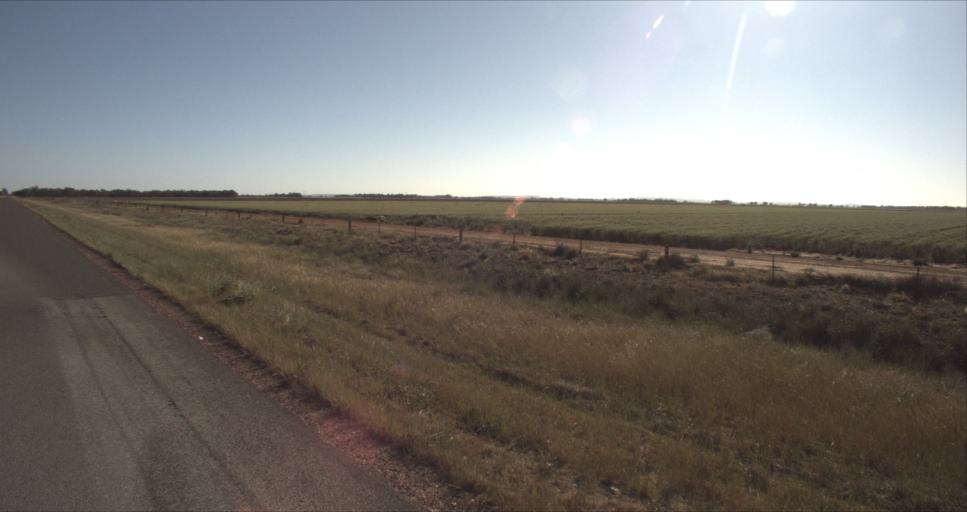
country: AU
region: New South Wales
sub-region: Leeton
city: Leeton
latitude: -34.5744
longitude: 146.2628
